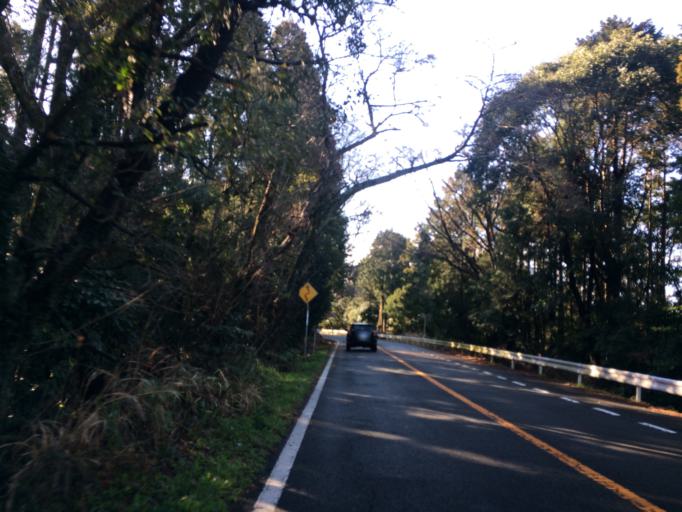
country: JP
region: Shizuoka
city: Shizuoka-shi
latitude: 34.9761
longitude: 138.4472
